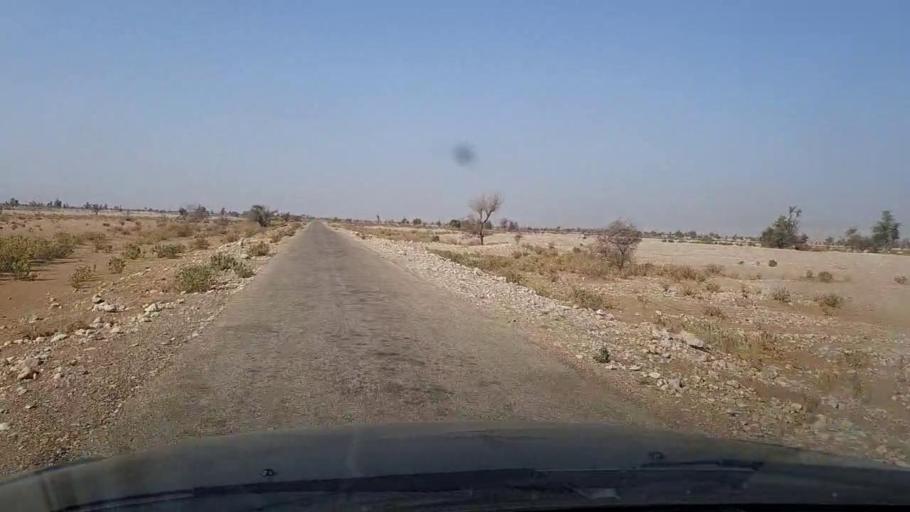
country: PK
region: Sindh
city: Sann
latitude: 25.9331
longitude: 68.0238
